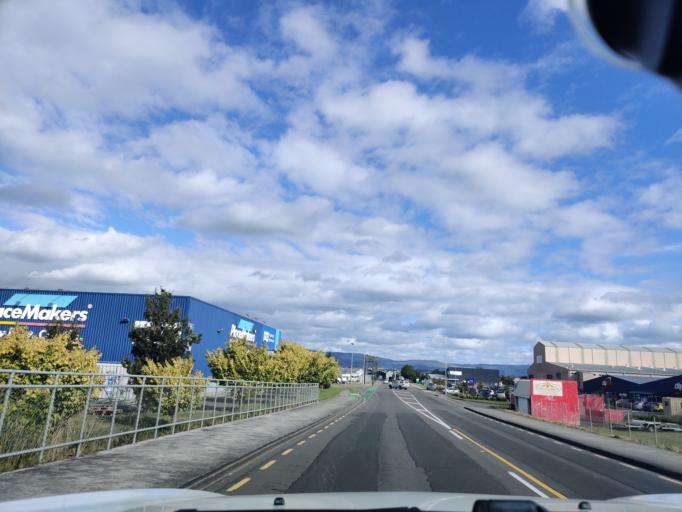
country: NZ
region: Manawatu-Wanganui
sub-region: Palmerston North City
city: Palmerston North
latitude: -40.3273
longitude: 175.6268
